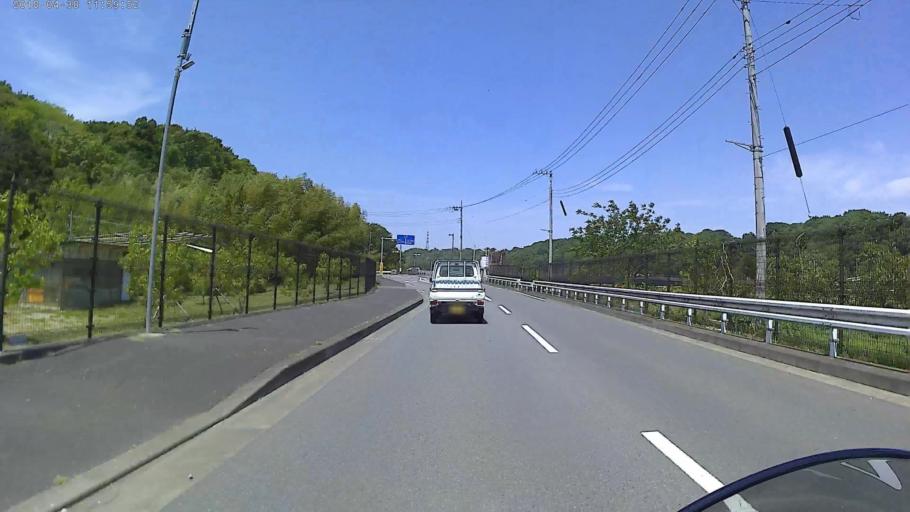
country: JP
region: Kanagawa
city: Zama
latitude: 35.5106
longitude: 139.3286
